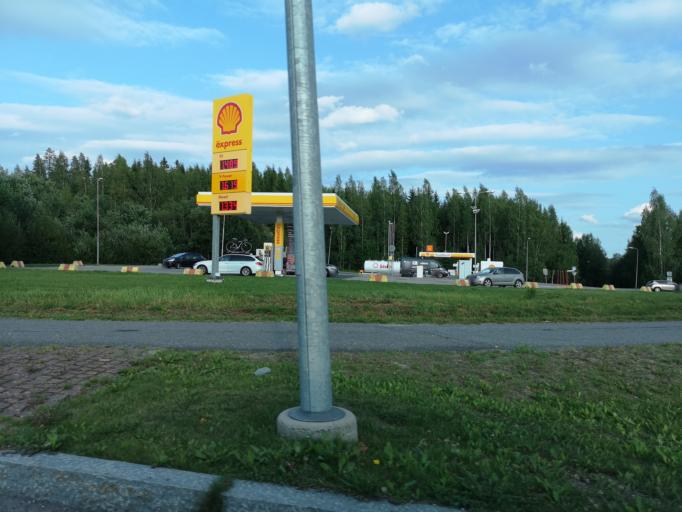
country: FI
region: Paijanne Tavastia
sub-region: Lahti
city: Lahti
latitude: 60.9840
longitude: 25.7379
